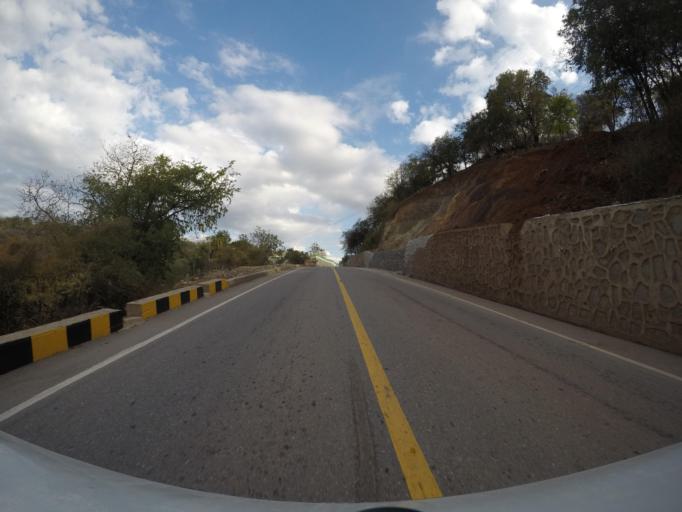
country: TL
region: Bobonaro
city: Maliana
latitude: -8.8477
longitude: 125.0598
